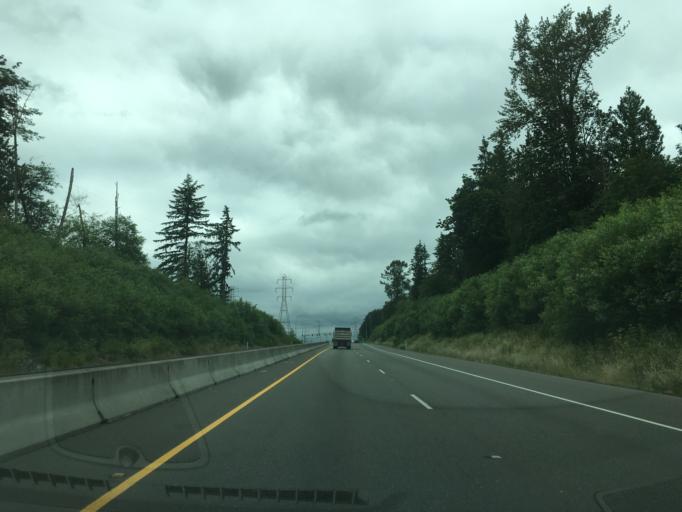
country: US
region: Washington
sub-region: Snohomish County
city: West Lake Stevens
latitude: 48.0177
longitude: -122.1088
